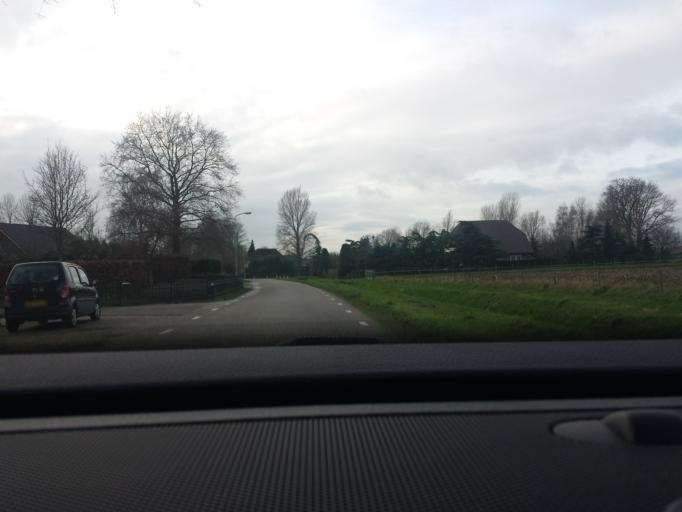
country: NL
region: Gelderland
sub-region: Gemeente Zevenaar
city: Zevenaar
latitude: 51.9271
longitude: 6.1370
